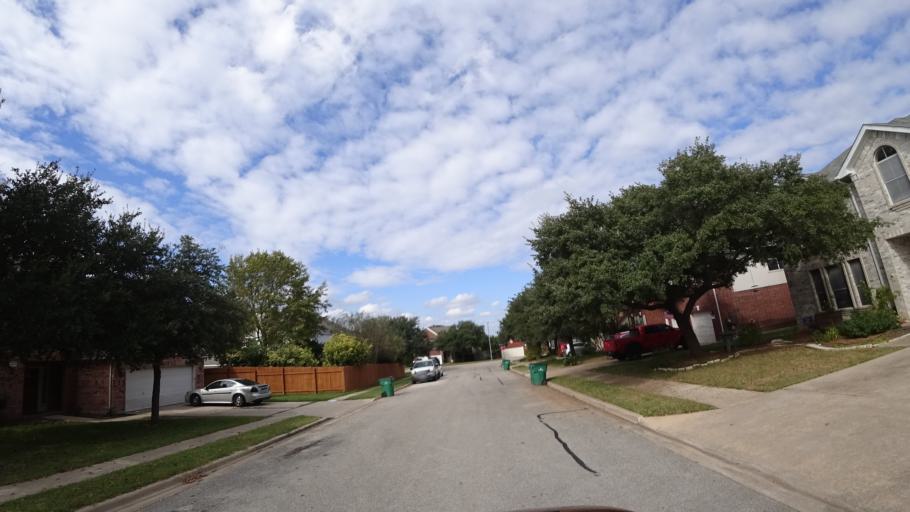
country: US
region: Texas
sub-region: Travis County
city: Windemere
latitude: 30.4409
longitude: -97.6427
